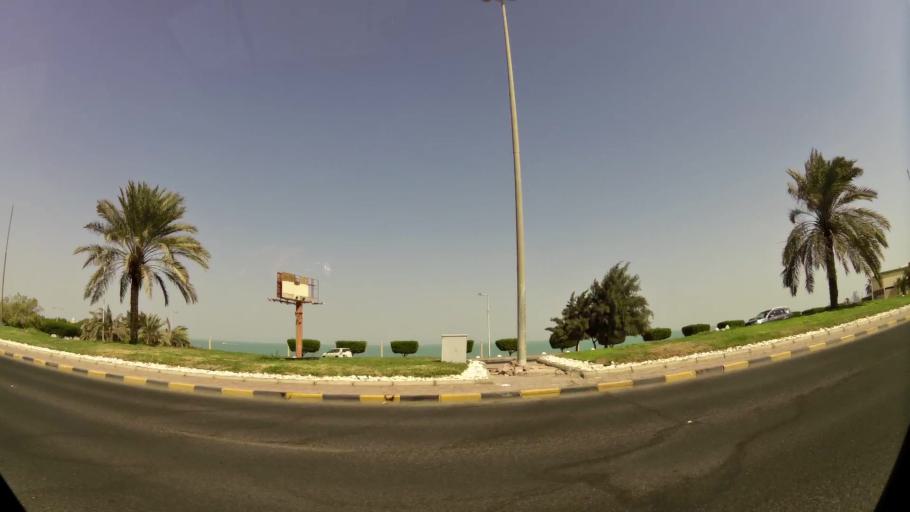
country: KW
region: Muhafazat Hawalli
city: Hawalli
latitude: 29.3454
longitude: 48.0419
